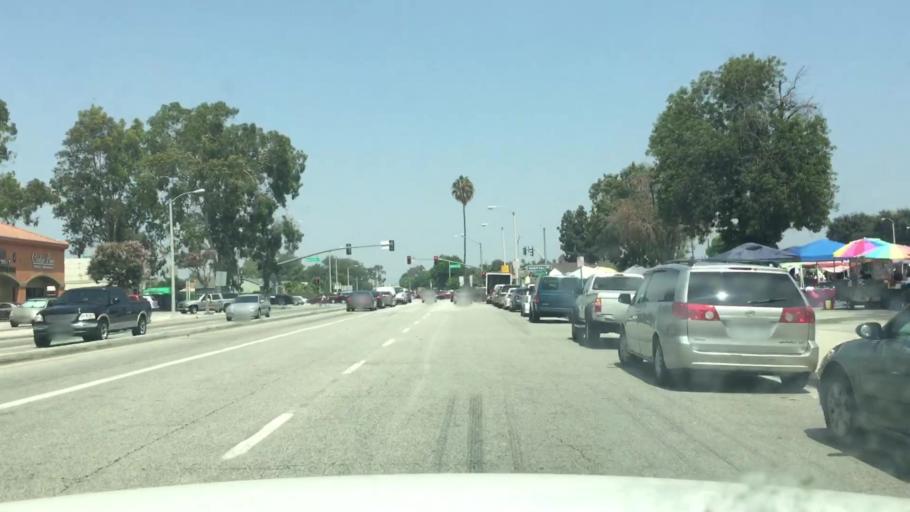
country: US
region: California
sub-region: Los Angeles County
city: West Whittier-Los Nietos
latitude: 33.9725
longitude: -118.0795
